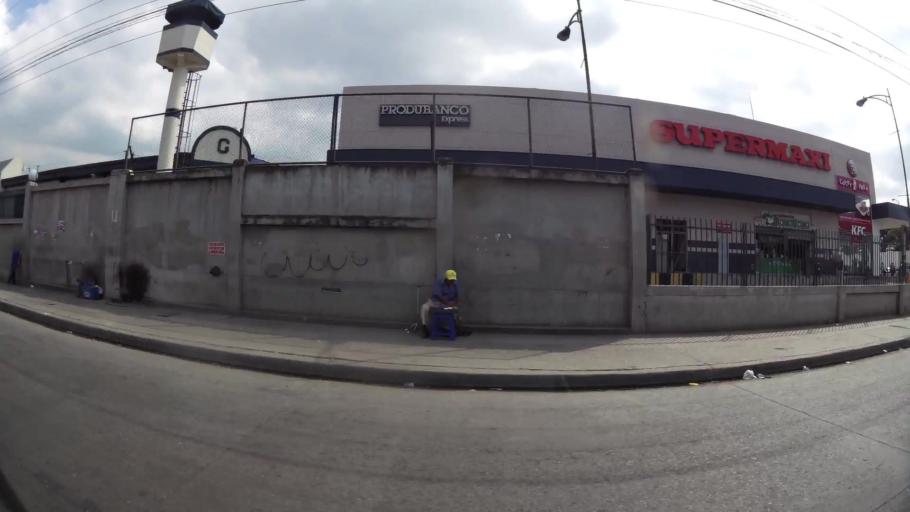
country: EC
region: Guayas
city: Santa Lucia
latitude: -2.0959
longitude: -79.9364
